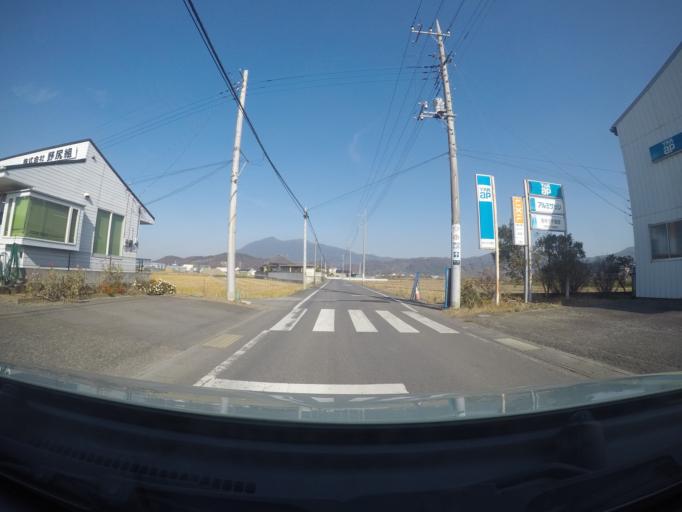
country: JP
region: Ibaraki
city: Tsukuba
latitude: 36.1656
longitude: 140.0891
